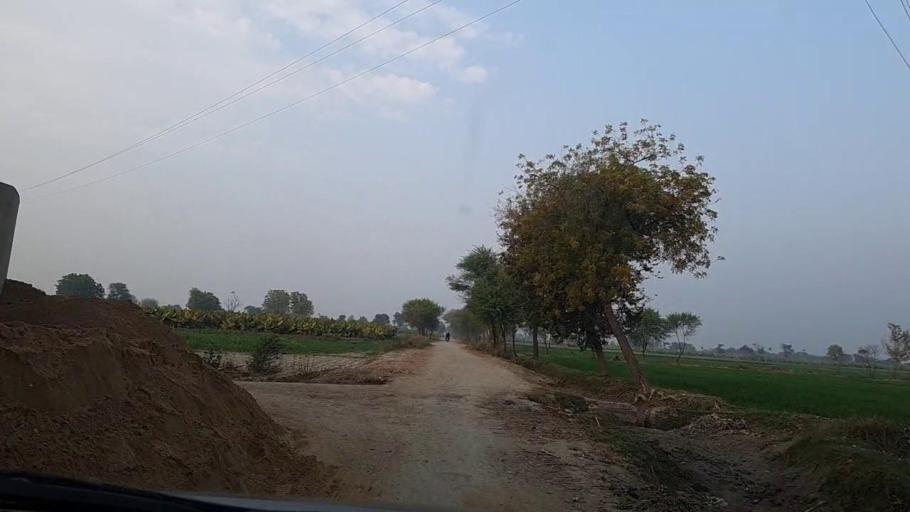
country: PK
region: Sindh
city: Nawabshah
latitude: 26.2855
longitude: 68.3211
